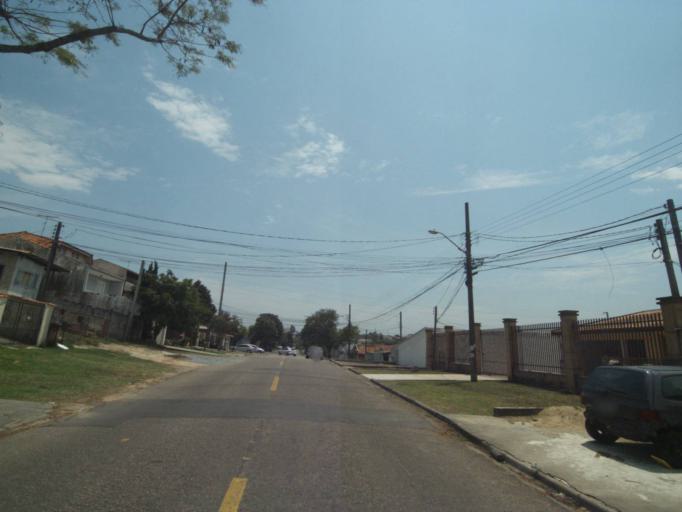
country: BR
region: Parana
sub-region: Pinhais
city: Pinhais
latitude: -25.4076
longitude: -49.2073
